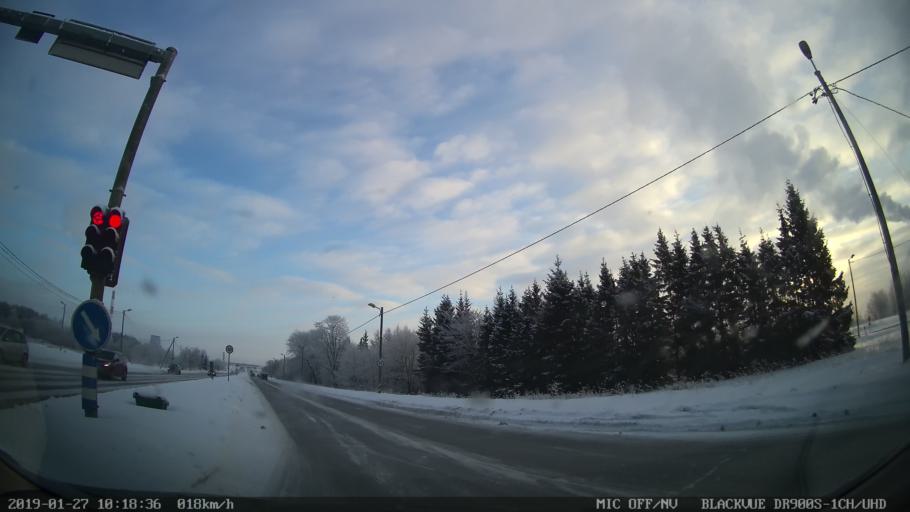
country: EE
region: Harju
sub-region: Tallinna linn
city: Kose
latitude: 59.4424
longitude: 24.9043
